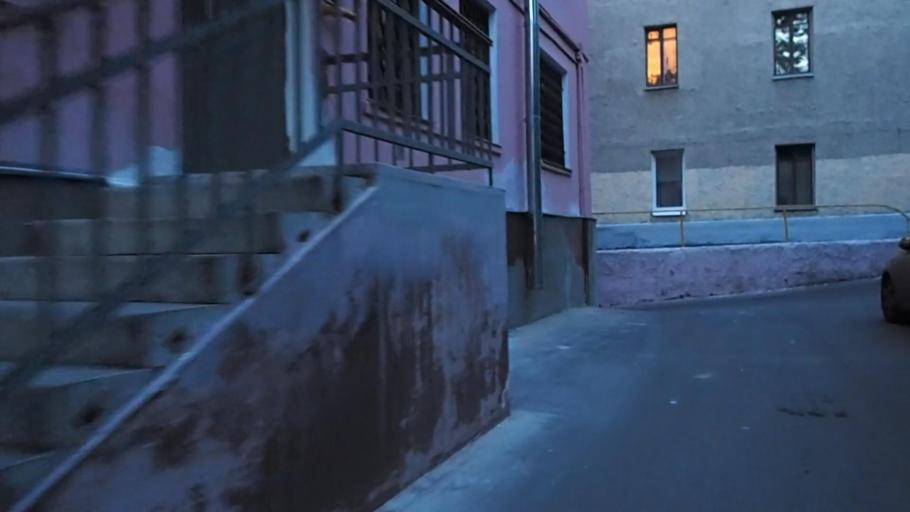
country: RU
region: Moscow
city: Sokol'niki
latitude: 55.7965
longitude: 37.6903
